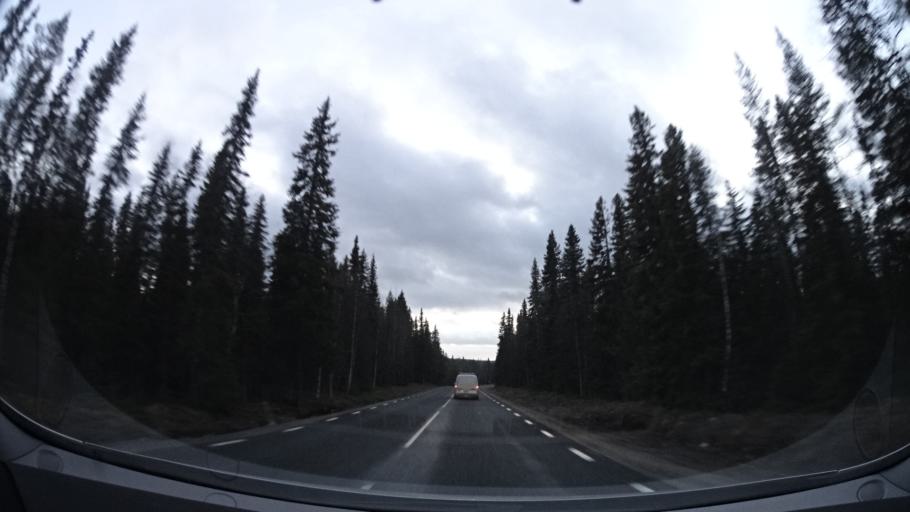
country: SE
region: Vaesterbotten
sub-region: Asele Kommun
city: Insjon
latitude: 64.2820
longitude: 17.6121
